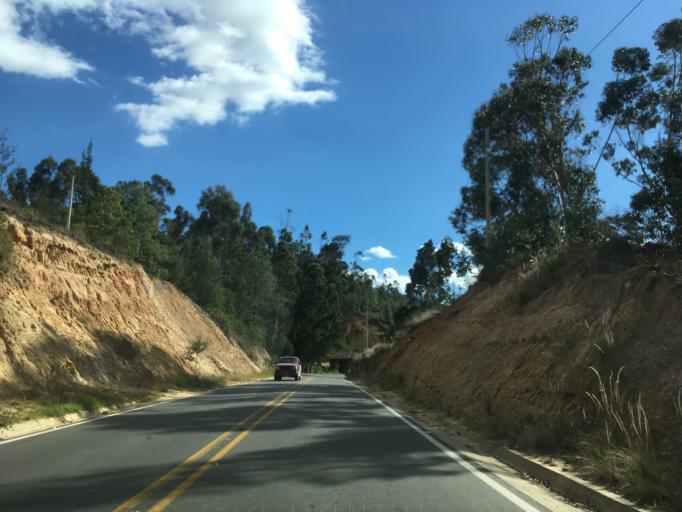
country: CO
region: Boyaca
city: Pesca
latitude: 5.5855
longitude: -73.0324
